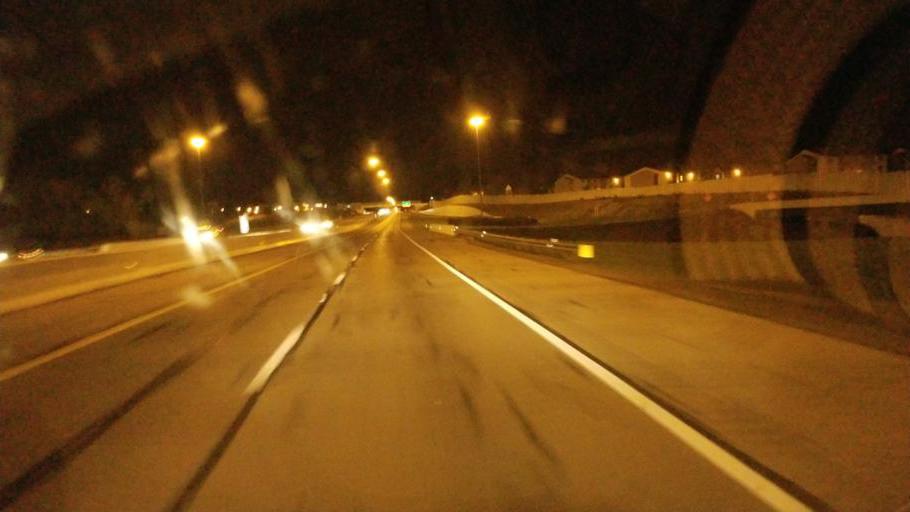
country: US
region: Ohio
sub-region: Montgomery County
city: Vandalia
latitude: 39.8654
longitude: -84.1902
